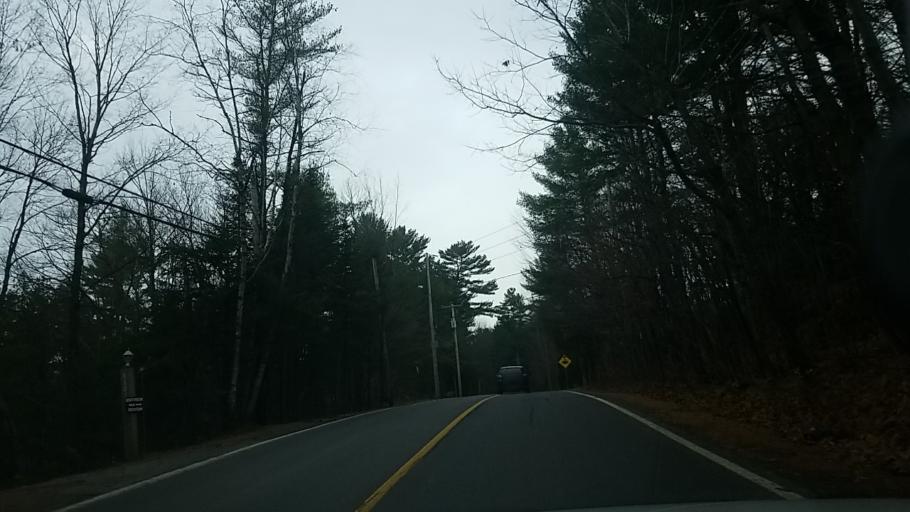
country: CA
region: Quebec
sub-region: Laurentides
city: Saint-Colomban
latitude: 45.7828
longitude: -74.1009
